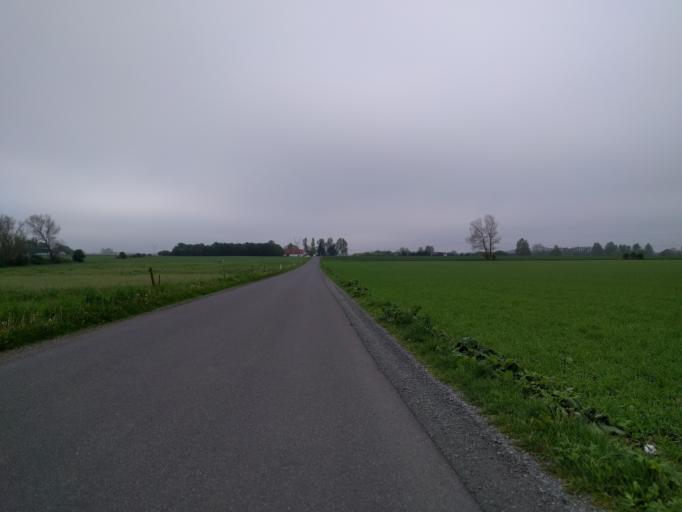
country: DK
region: South Denmark
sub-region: Odense Kommune
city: Bullerup
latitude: 55.3907
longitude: 10.5151
